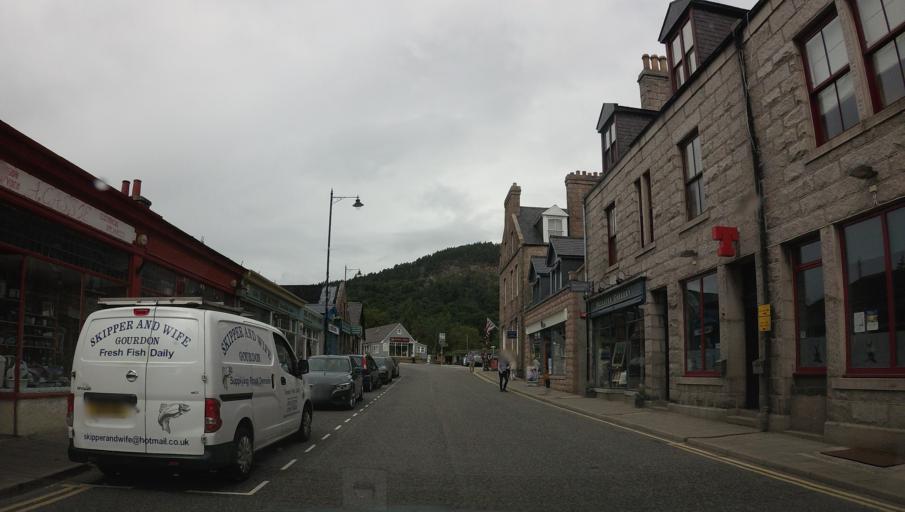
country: GB
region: Scotland
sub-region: Aberdeenshire
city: Ballater
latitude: 57.0494
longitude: -3.0404
